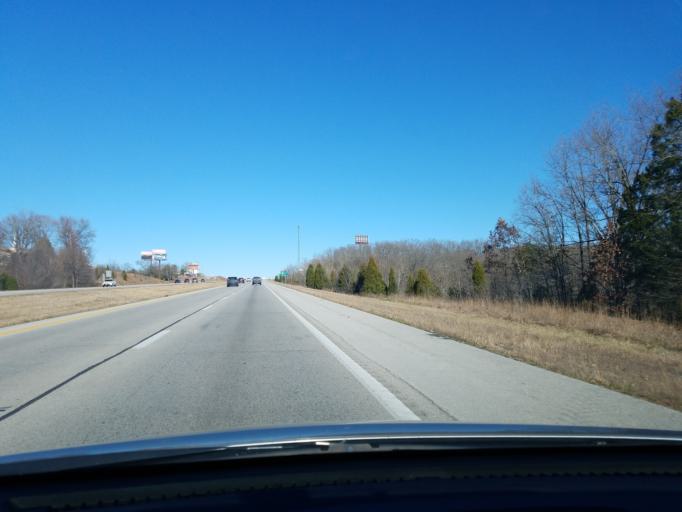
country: US
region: Missouri
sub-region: Taney County
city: Merriam Woods
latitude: 36.8004
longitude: -93.2263
